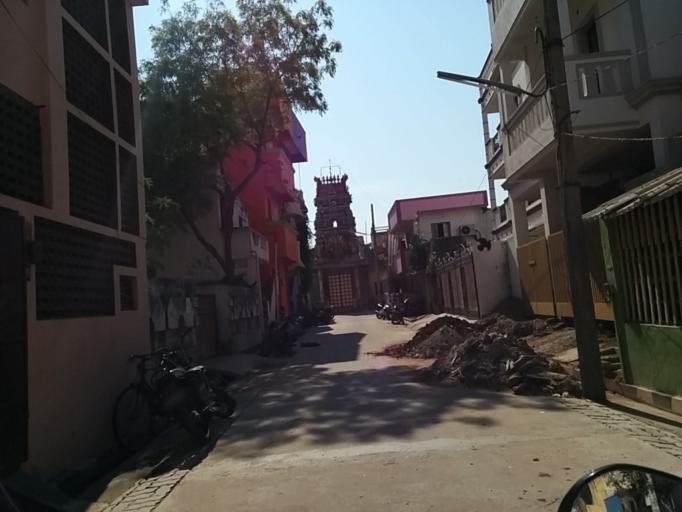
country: IN
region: Pondicherry
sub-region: Puducherry
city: Puducherry
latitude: 11.9460
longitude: 79.8366
